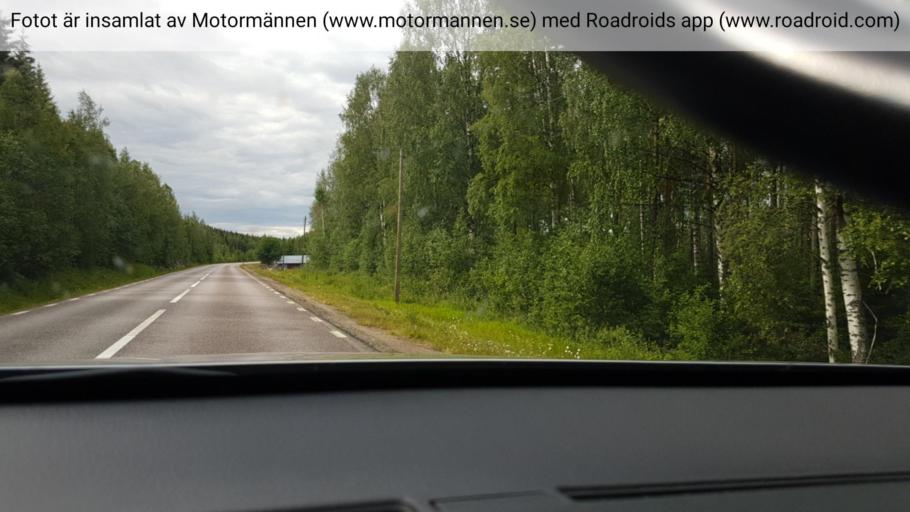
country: NO
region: Hedmark
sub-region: Trysil
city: Innbygda
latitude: 60.9031
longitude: 12.5683
